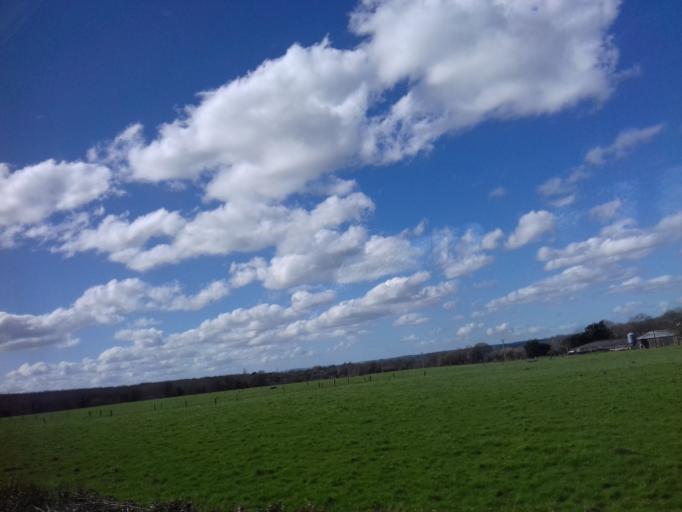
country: IE
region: Munster
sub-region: County Cork
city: Kanturk
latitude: 52.1186
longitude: -8.7940
